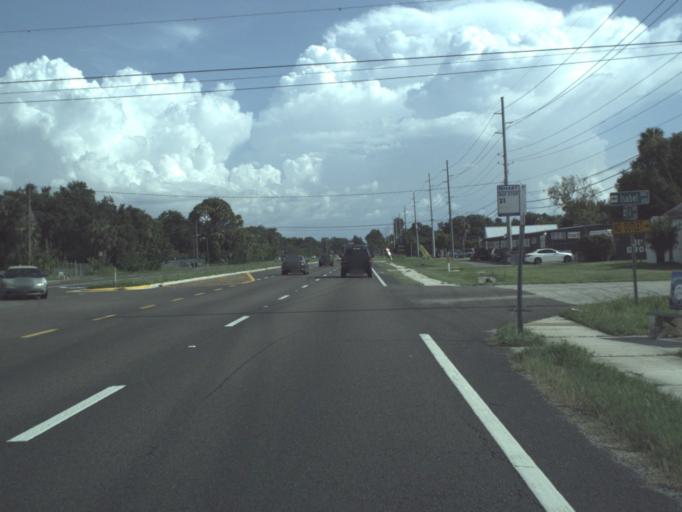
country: US
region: Florida
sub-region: Hillsborough County
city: Gibsonton
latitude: 27.8315
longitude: -82.3819
